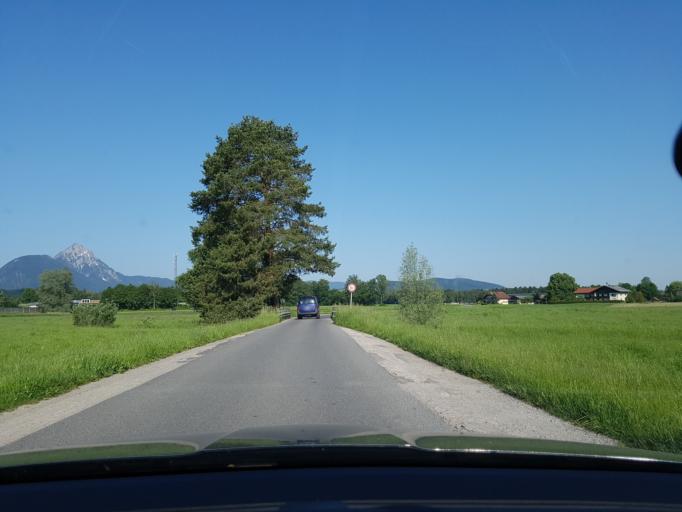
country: AT
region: Salzburg
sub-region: Politischer Bezirk Salzburg-Umgebung
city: Grodig
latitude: 47.7682
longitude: 12.9954
